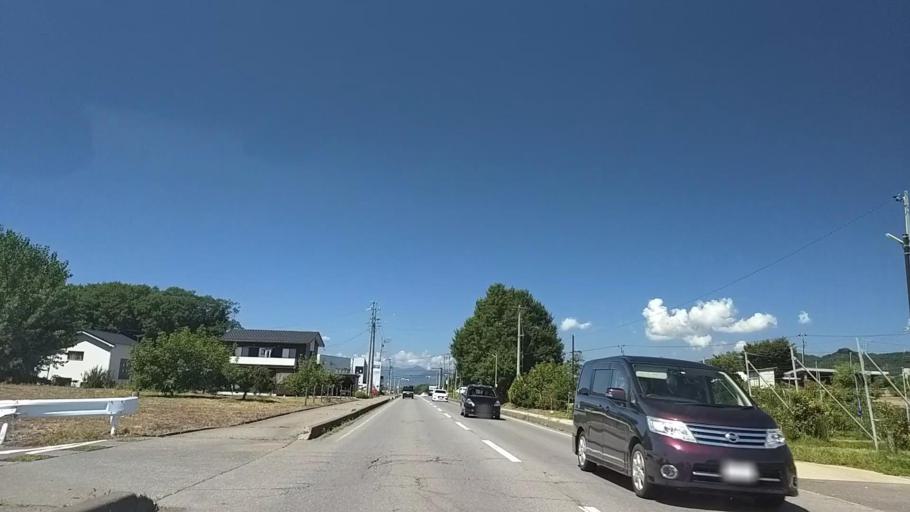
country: JP
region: Nagano
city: Komoro
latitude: 36.3605
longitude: 138.3621
